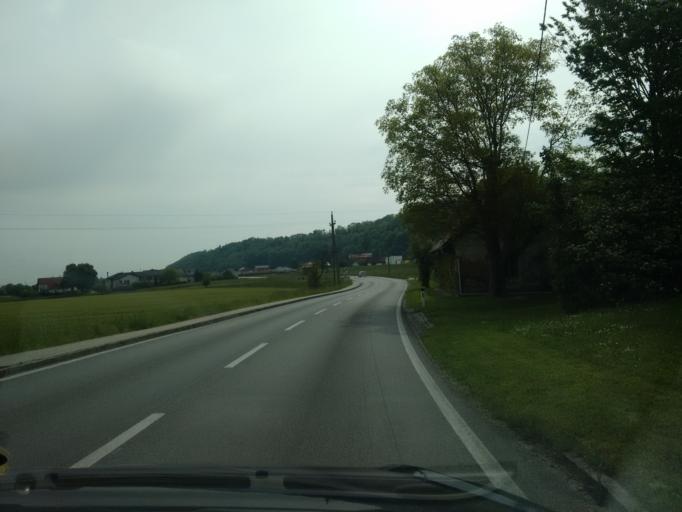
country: AT
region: Upper Austria
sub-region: Politischer Bezirk Linz-Land
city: Horsching
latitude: 48.1889
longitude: 14.1899
